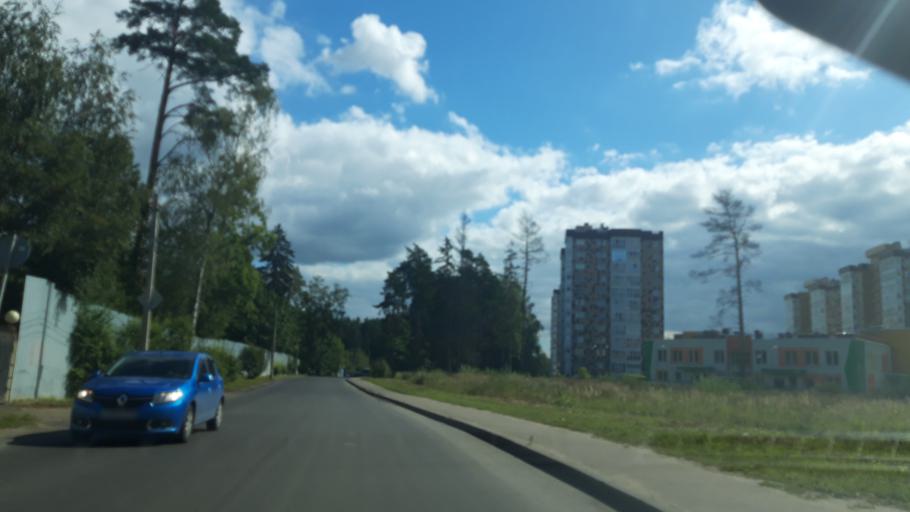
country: RU
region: Moskovskaya
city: Andreyevka
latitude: 55.9827
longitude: 37.1086
